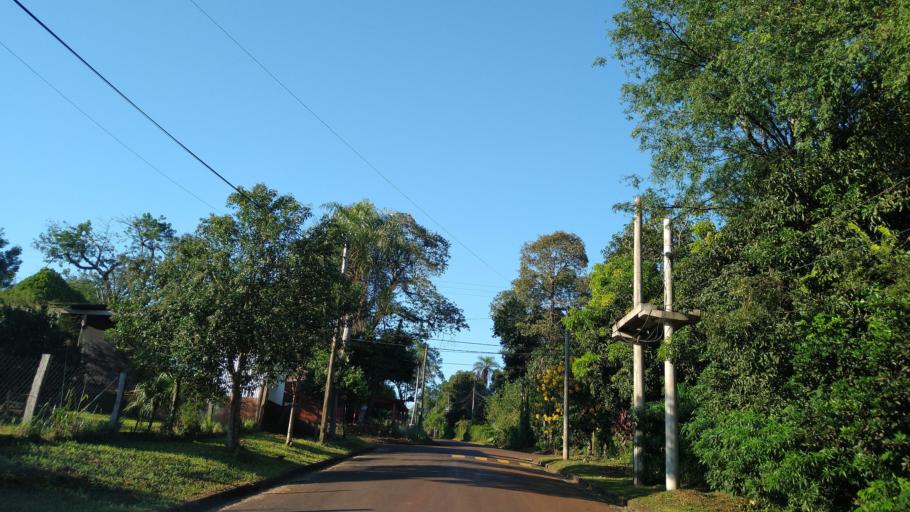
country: AR
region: Misiones
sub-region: Departamento de Montecarlo
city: Montecarlo
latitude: -26.5643
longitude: -54.7689
